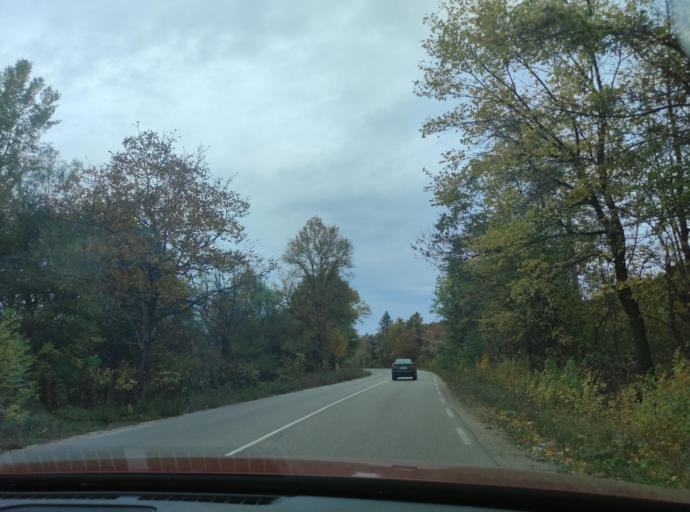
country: BG
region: Montana
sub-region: Obshtina Berkovitsa
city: Berkovitsa
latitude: 43.2668
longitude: 23.1753
